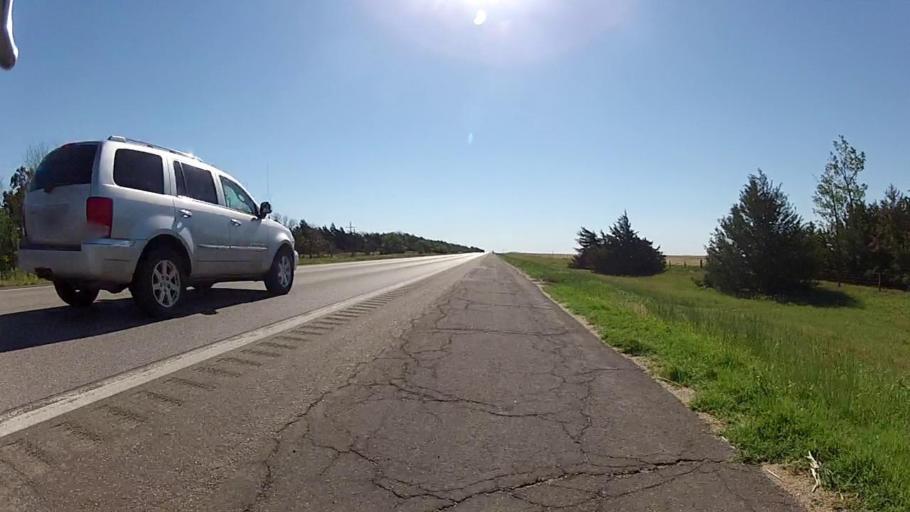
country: US
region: Kansas
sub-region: Kiowa County
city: Greensburg
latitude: 37.5865
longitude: -99.5837
